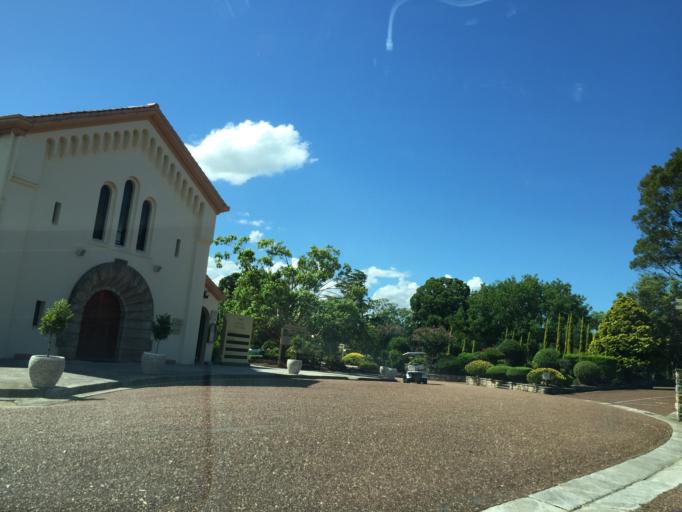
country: AU
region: New South Wales
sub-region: Willoughby
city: Chatswood West
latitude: -33.7954
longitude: 151.1532
